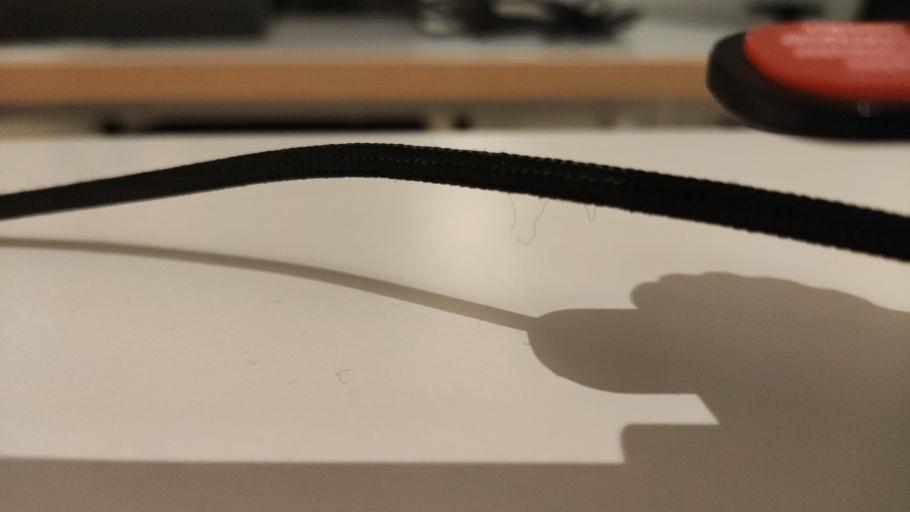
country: RU
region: Moskovskaya
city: Semkhoz
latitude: 56.3877
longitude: 38.0543
